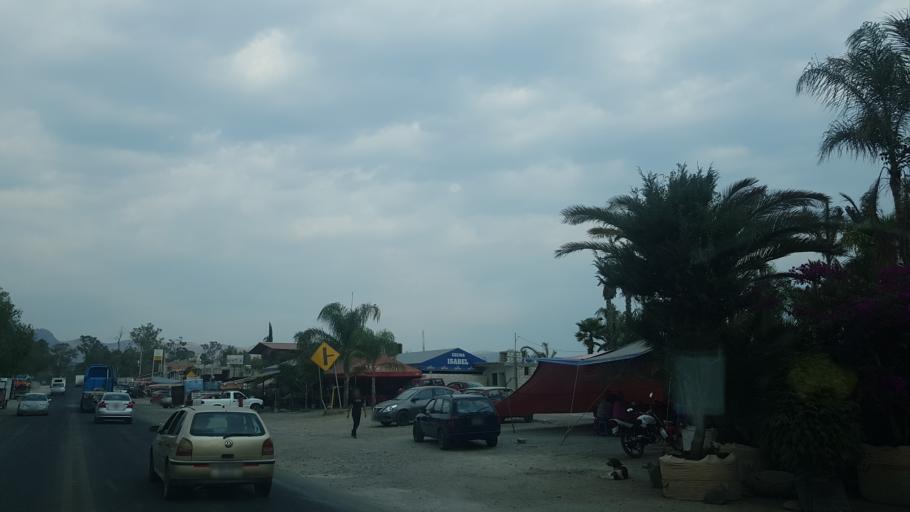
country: MX
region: Puebla
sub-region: Santa Isabel Cholula
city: Santa Ana Acozautla
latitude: 18.9436
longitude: -98.3945
